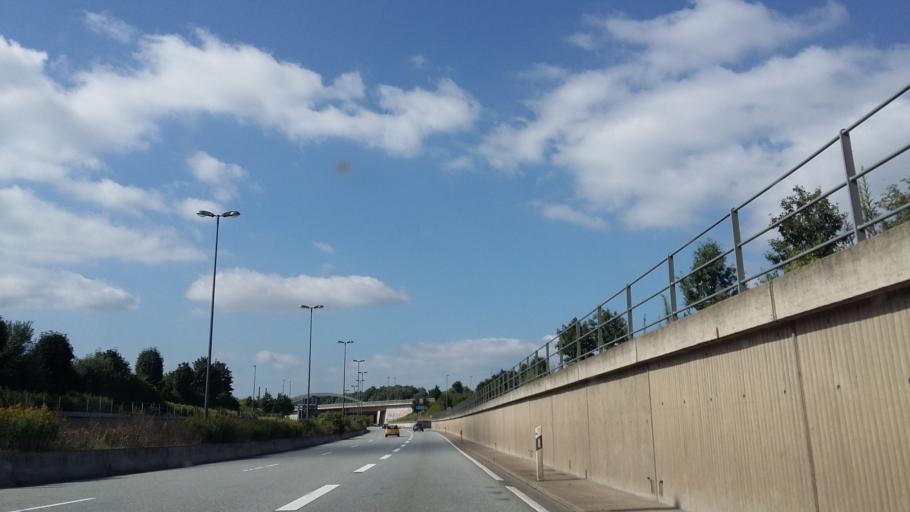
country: DE
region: Bremen
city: Bremen
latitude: 53.0666
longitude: 8.7772
